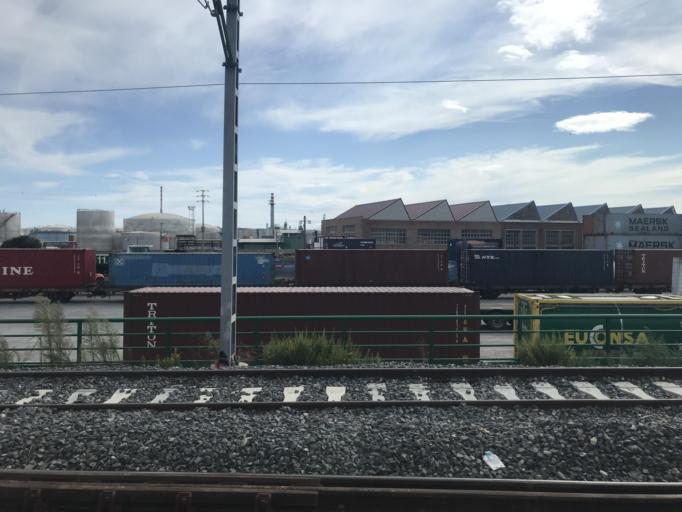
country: ES
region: Catalonia
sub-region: Provincia de Tarragona
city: Tarragona
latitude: 41.1111
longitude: 1.2143
